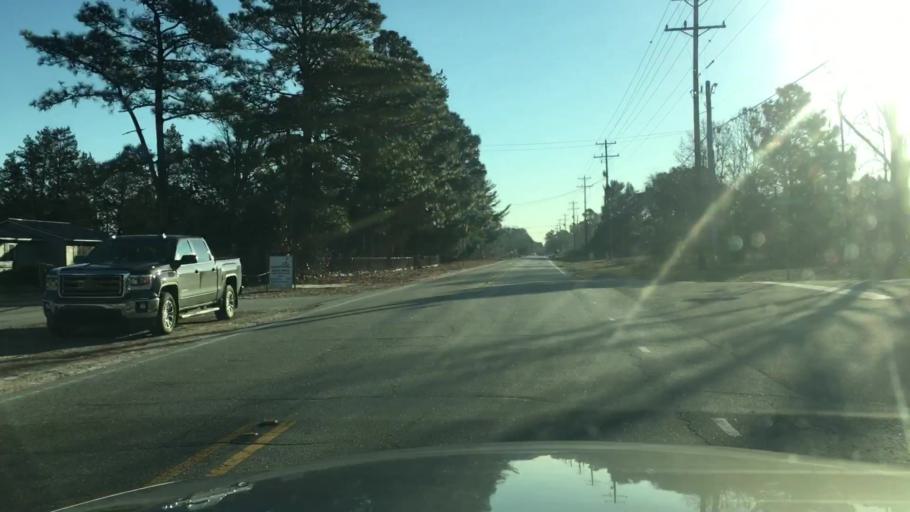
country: US
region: North Carolina
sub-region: Cumberland County
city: Hope Mills
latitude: 34.9767
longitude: -78.9817
